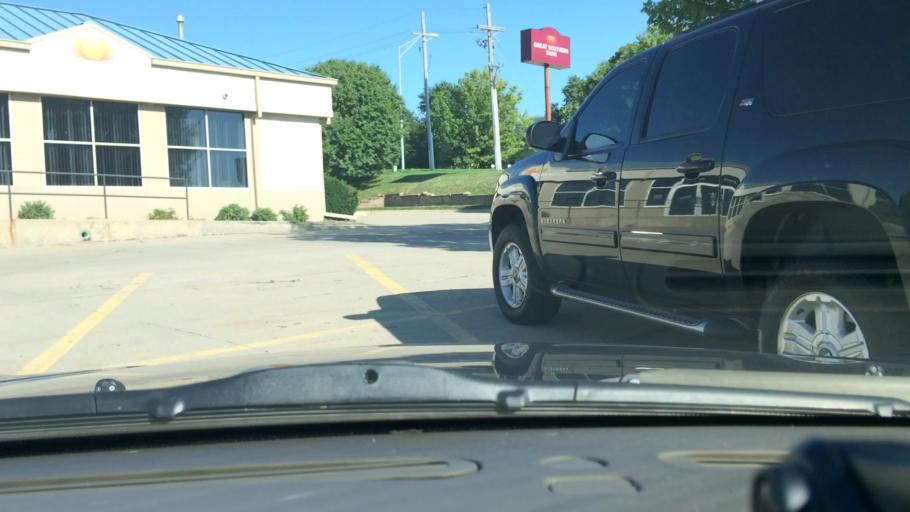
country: US
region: Nebraska
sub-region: Douglas County
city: Ralston
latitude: 41.2048
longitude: -96.0641
